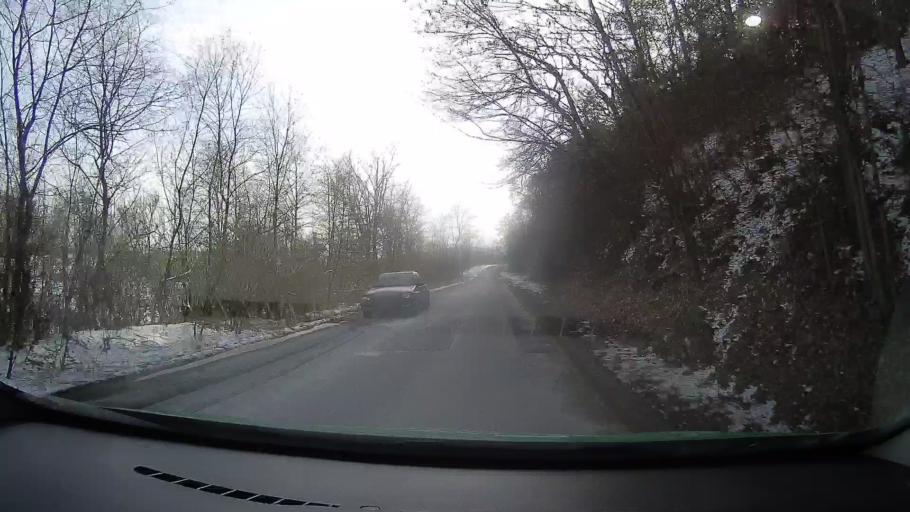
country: RO
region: Mures
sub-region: Comuna Apold
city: Saes
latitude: 46.1893
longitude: 24.7636
